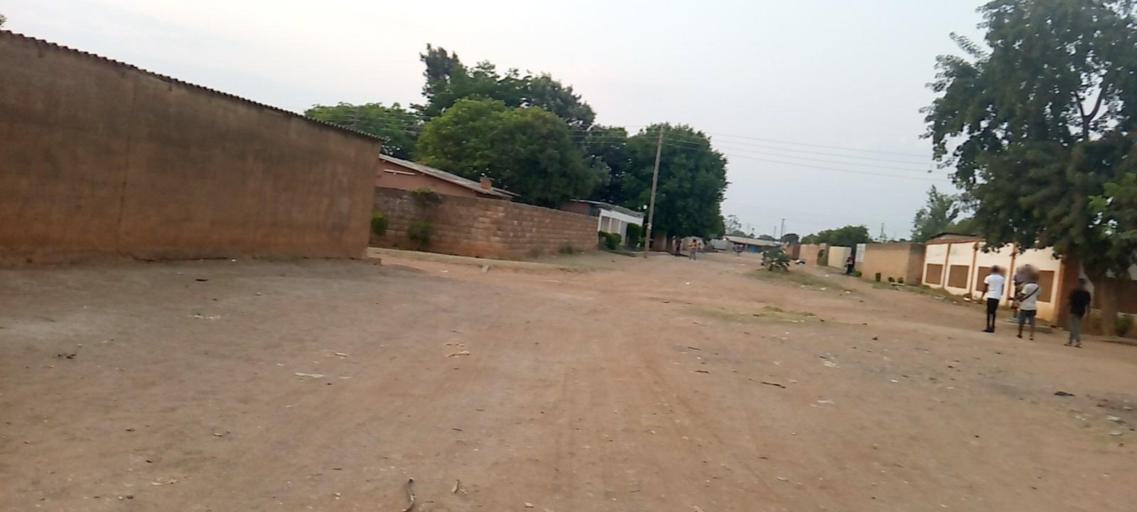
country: ZM
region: Lusaka
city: Lusaka
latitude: -15.4067
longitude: 28.3479
